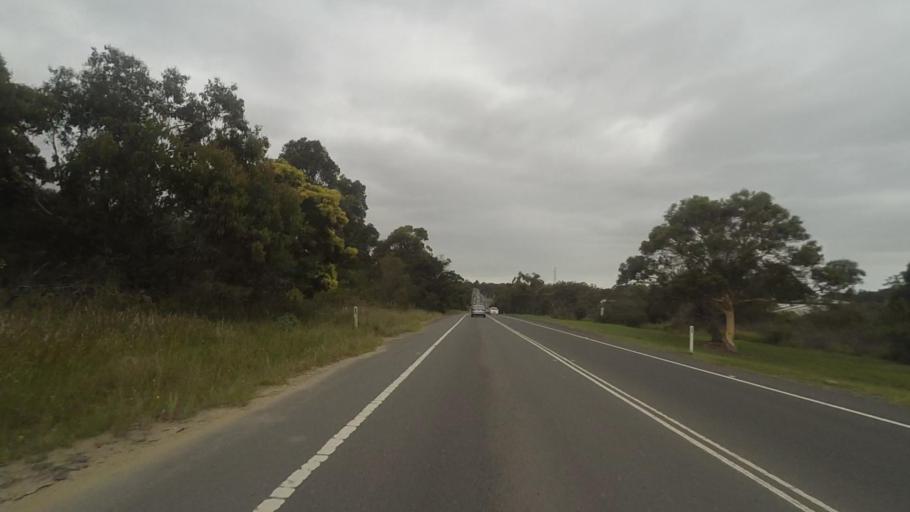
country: AU
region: New South Wales
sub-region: Sutherland Shire
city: Engadine
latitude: -34.0477
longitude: 150.9828
